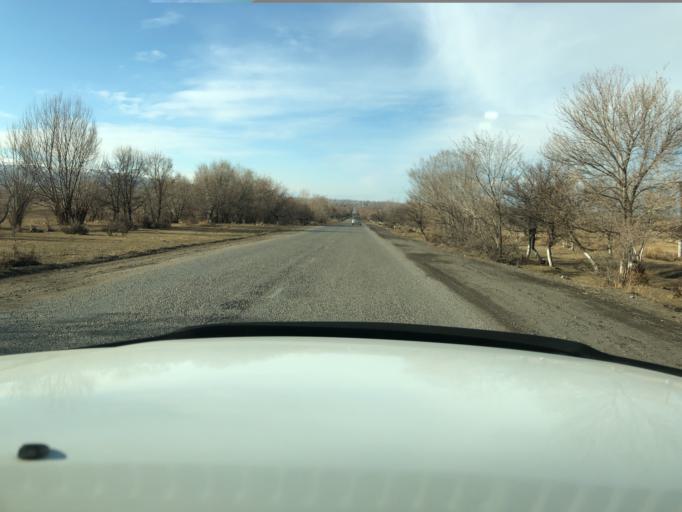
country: KG
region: Ysyk-Koel
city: Pokrovka
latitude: 42.3304
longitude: 77.9694
